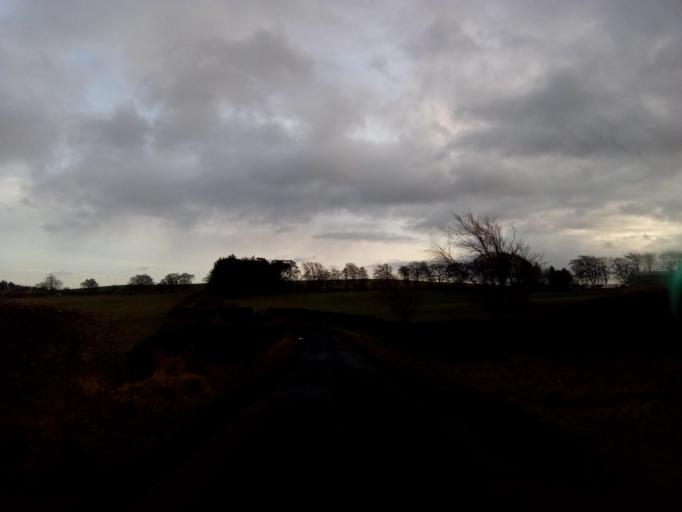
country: GB
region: Scotland
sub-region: The Scottish Borders
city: Selkirk
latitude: 55.5516
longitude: -2.7739
